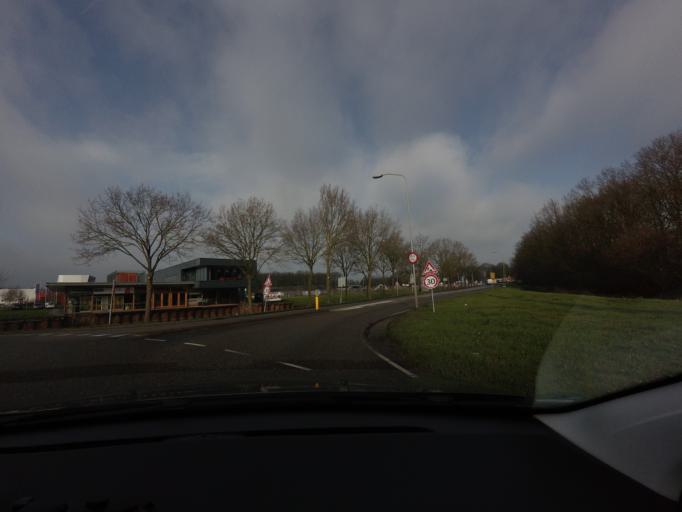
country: NL
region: Drenthe
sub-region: Gemeente Westerveld
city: Dwingeloo
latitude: 52.8563
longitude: 6.5006
